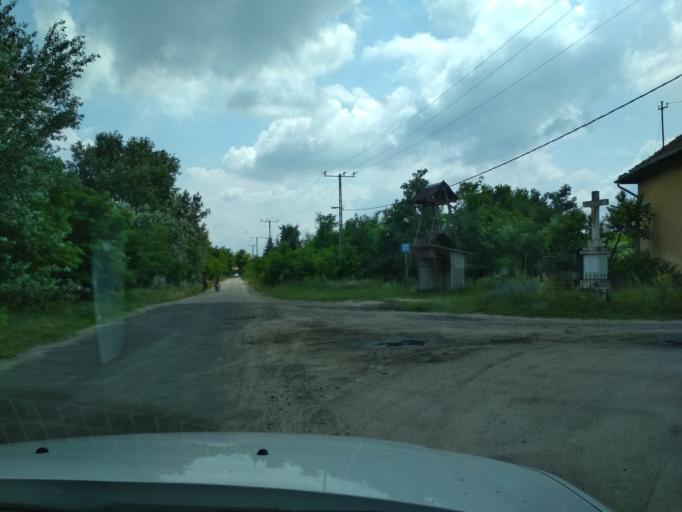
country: HU
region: Pest
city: Tapioszentmarton
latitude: 47.3750
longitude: 19.7560
